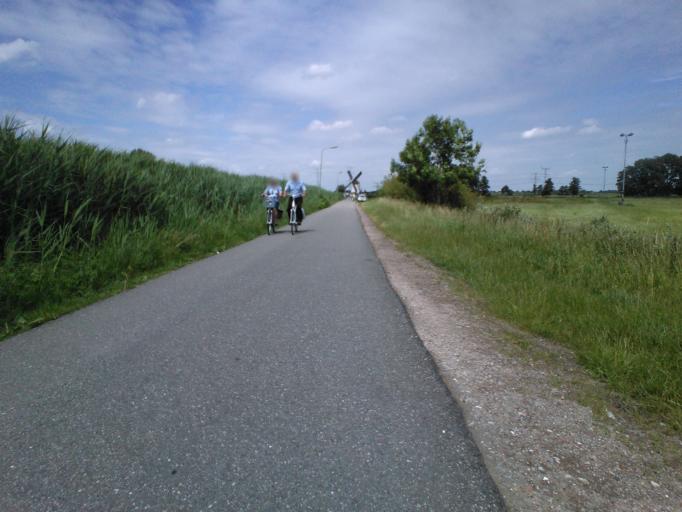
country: NL
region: South Holland
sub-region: Gemeente Alblasserdam
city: Alblasserdam
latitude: 51.8694
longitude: 4.6736
